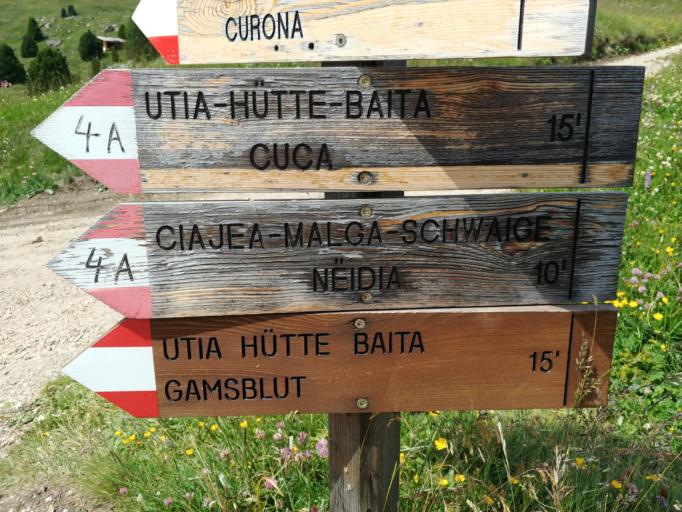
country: IT
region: Trentino-Alto Adige
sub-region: Bolzano
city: Santa Cristina Valgardena
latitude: 46.5897
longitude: 11.7432
